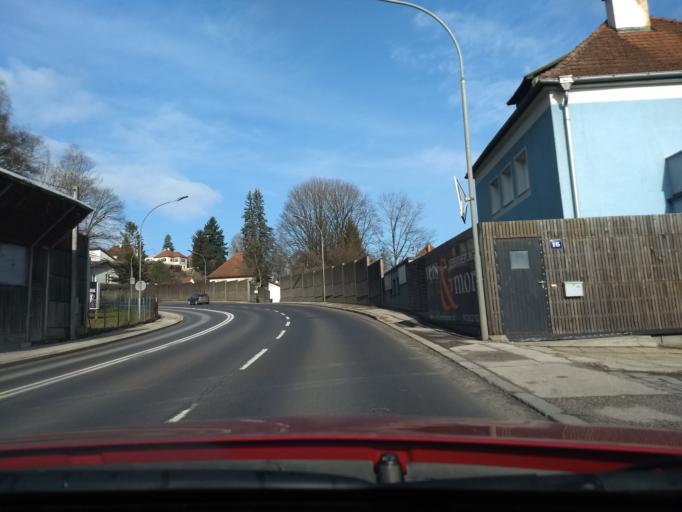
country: AT
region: Upper Austria
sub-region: Steyr Stadt
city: Steyr
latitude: 48.0482
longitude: 14.4267
